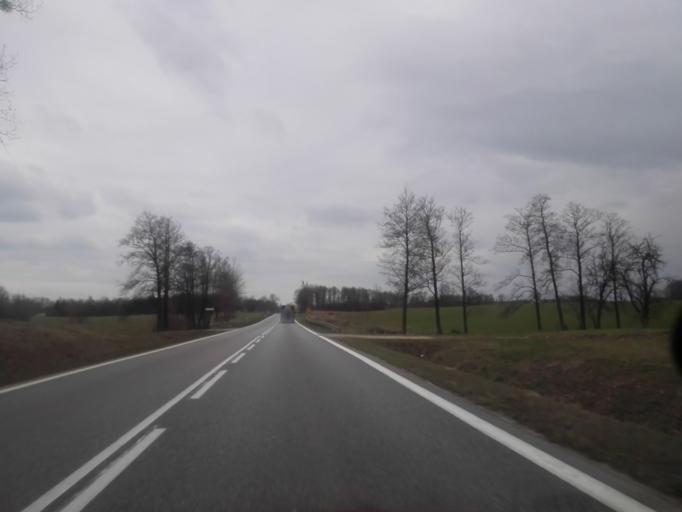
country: PL
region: Podlasie
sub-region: Powiat augustowski
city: Augustow
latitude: 53.8076
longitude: 22.9038
